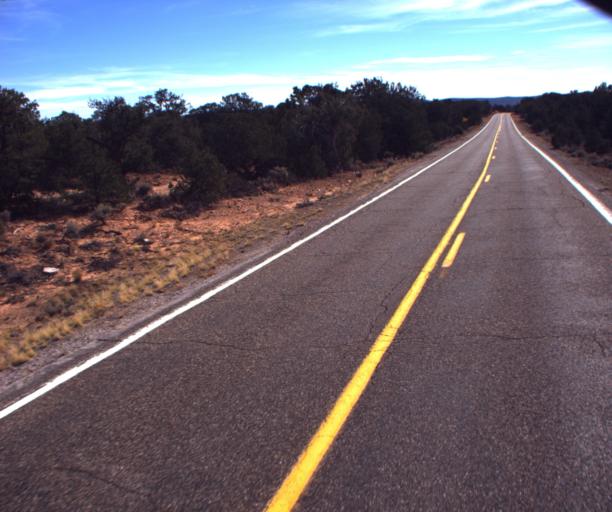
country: US
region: Arizona
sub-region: Navajo County
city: Kayenta
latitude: 36.6441
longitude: -110.5157
